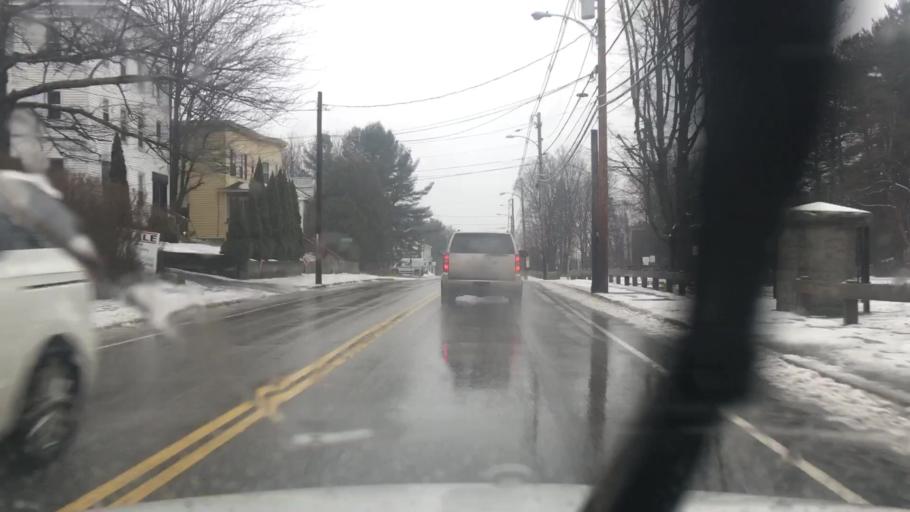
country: US
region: Maine
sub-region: York County
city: Biddeford
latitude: 43.4883
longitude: -70.4486
